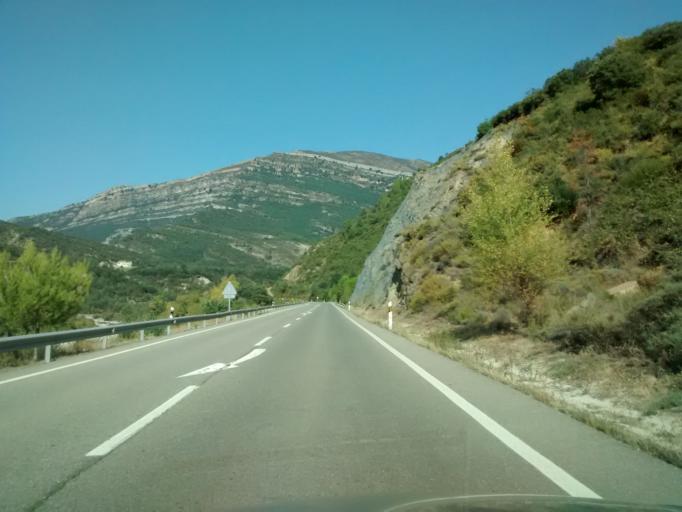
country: ES
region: Aragon
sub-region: Provincia de Huesca
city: Boltana
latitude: 42.4537
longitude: 0.0558
